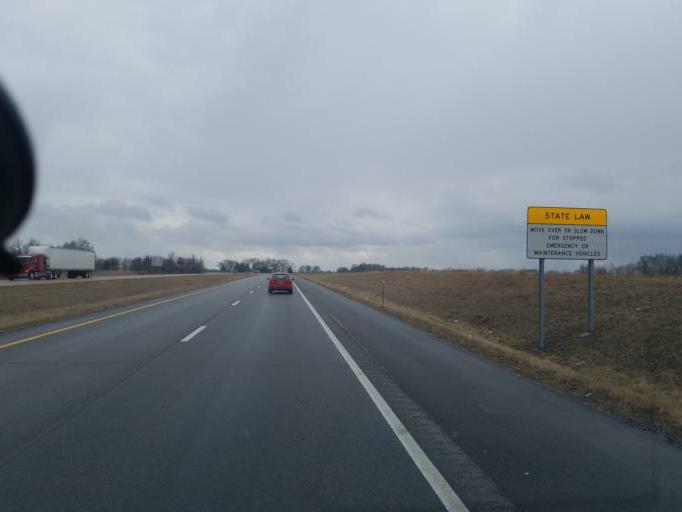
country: US
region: Missouri
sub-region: Randolph County
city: Moberly
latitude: 39.3823
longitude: -92.4138
